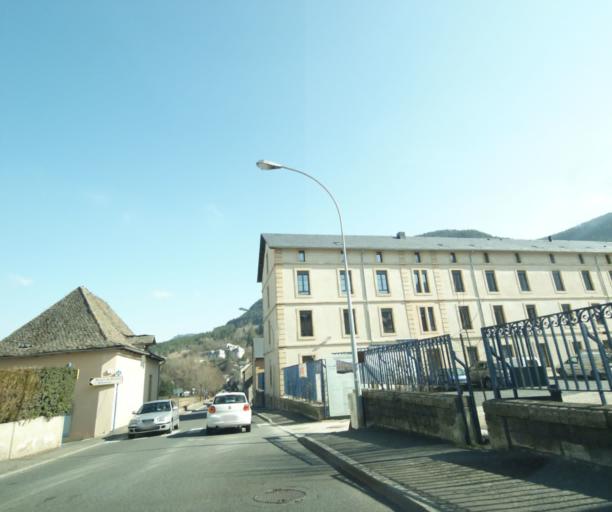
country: FR
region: Languedoc-Roussillon
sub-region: Departement de la Lozere
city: Mende
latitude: 44.5175
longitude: 3.5042
